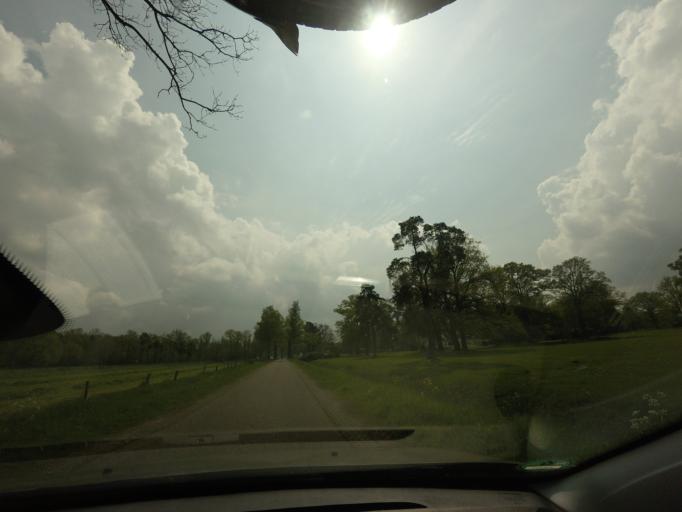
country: NL
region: Overijssel
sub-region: Gemeente Haaksbergen
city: Haaksbergen
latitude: 52.1762
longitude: 6.8108
